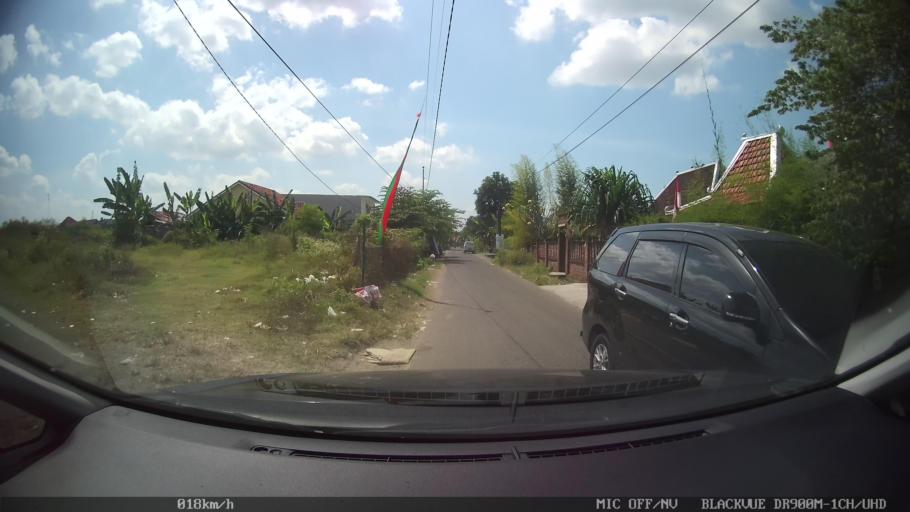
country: ID
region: Daerah Istimewa Yogyakarta
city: Yogyakarta
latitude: -7.8289
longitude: 110.3812
